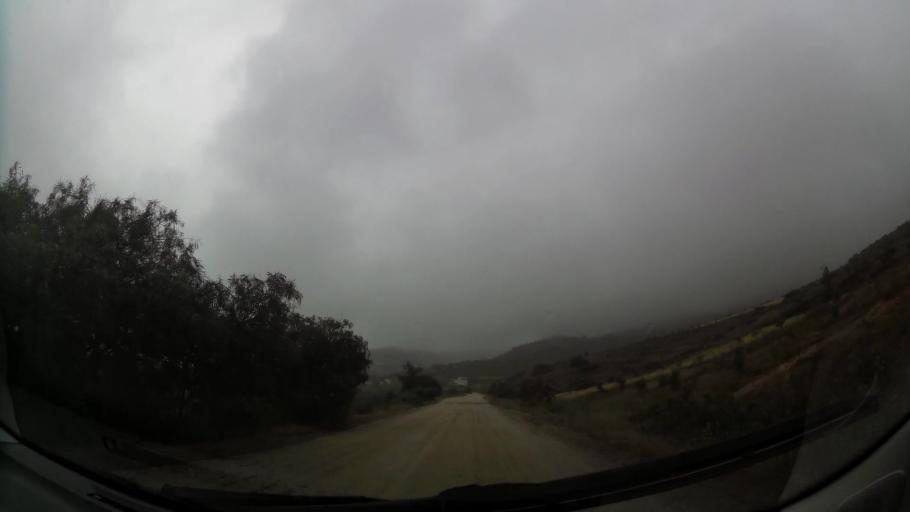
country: MA
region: Taza-Al Hoceima-Taounate
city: Imzourene
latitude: 35.1203
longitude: -3.7792
